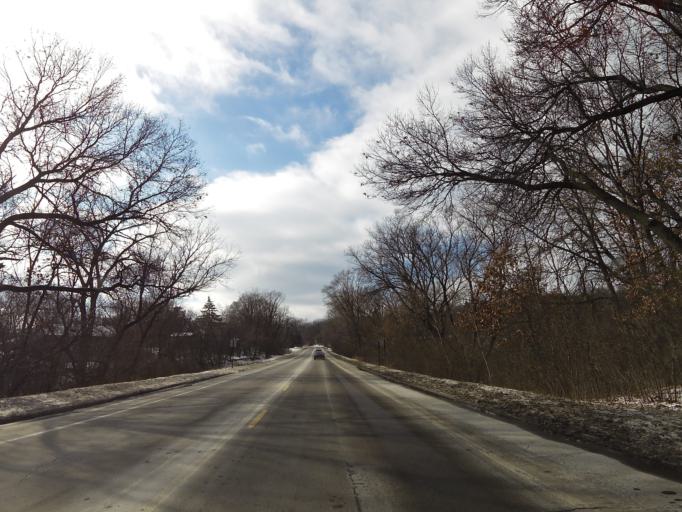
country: US
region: Minnesota
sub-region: Hennepin County
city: Minnetonka Mills
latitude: 44.9202
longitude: -93.4371
